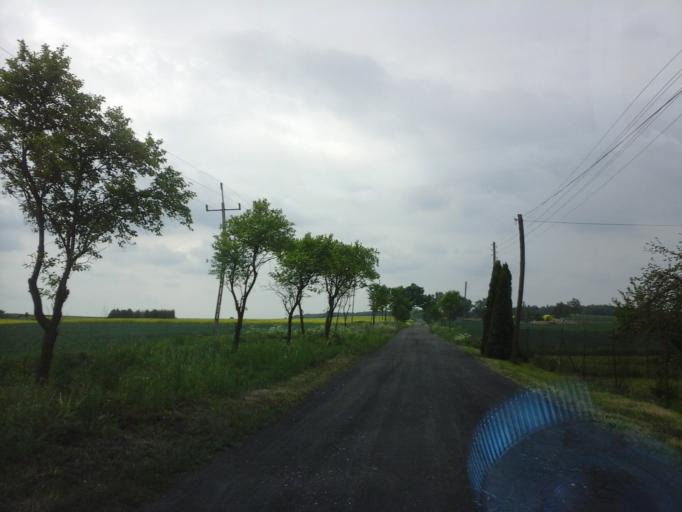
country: PL
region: West Pomeranian Voivodeship
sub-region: Powiat choszczenski
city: Pelczyce
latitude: 53.0157
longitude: 15.3704
